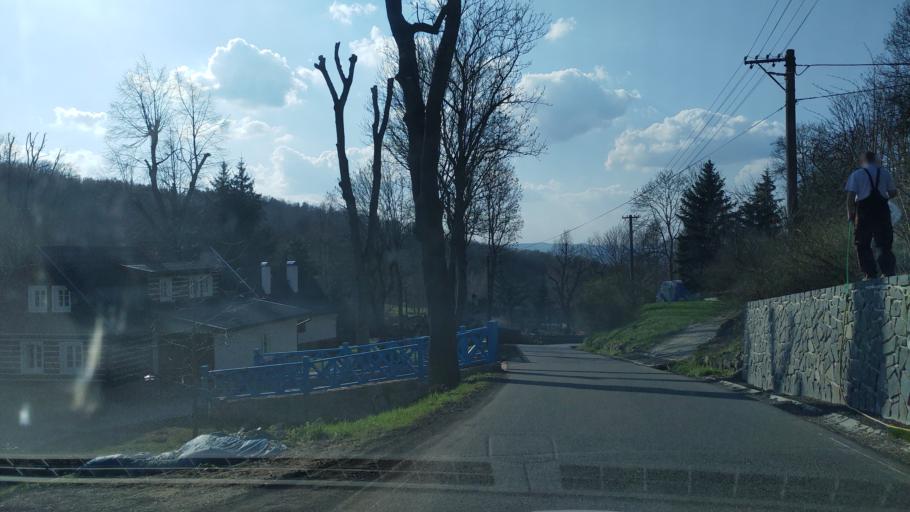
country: CZ
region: Ustecky
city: Vernerice
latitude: 50.6918
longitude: 14.2543
